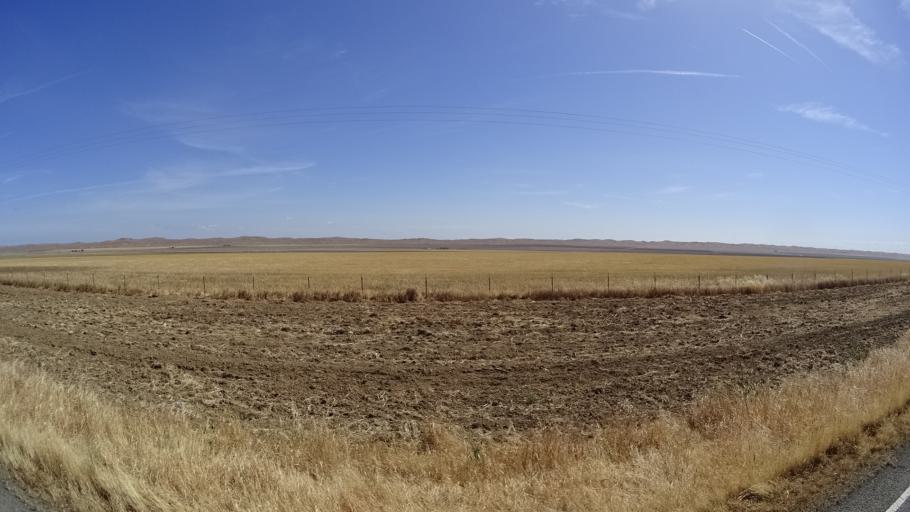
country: US
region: California
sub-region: Kings County
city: Avenal
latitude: 35.9296
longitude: -120.0804
